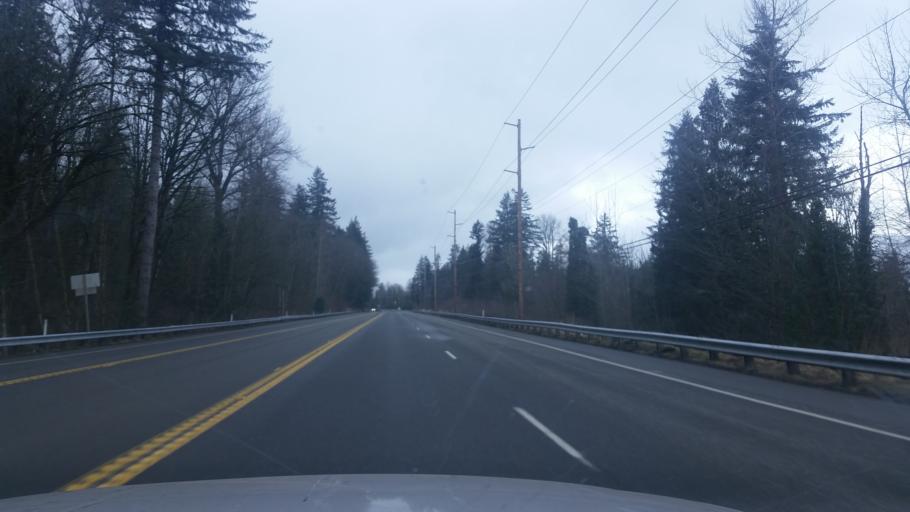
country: US
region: Washington
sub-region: King County
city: Snoqualmie
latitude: 47.5139
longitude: -121.8302
